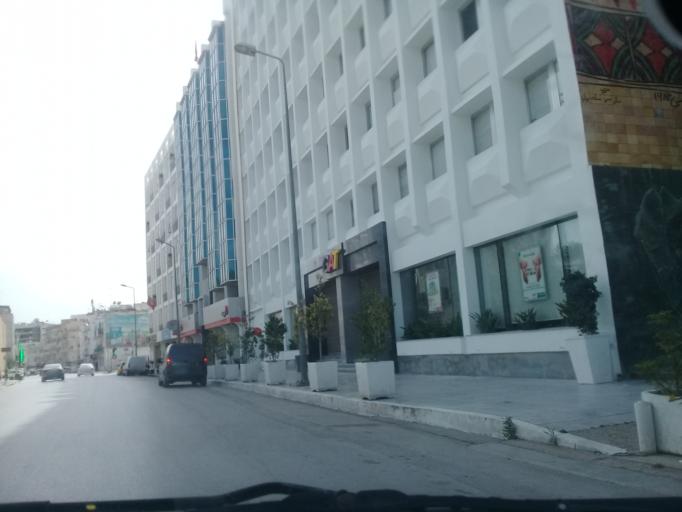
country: TN
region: Tunis
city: Tunis
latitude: 36.8179
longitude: 10.1826
